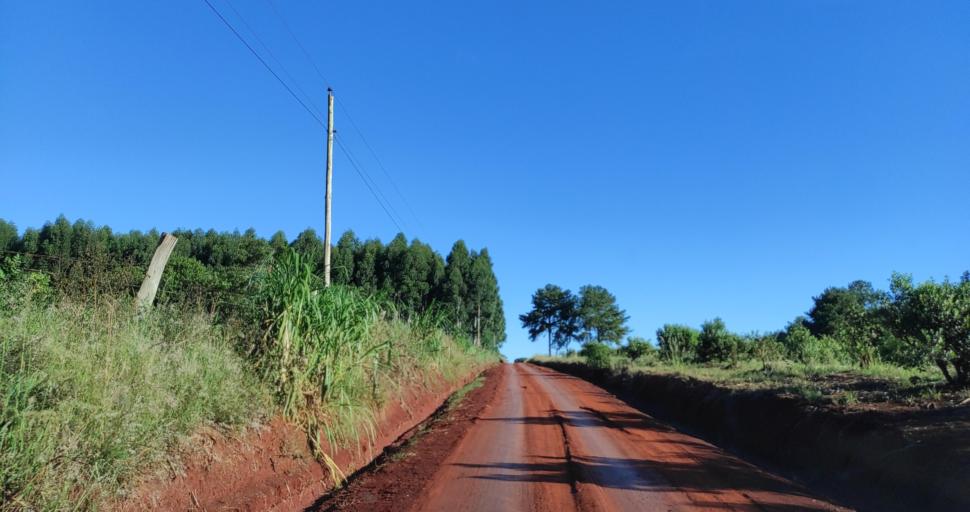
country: AR
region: Misiones
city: Puerto Rico
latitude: -26.8559
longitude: -55.0142
